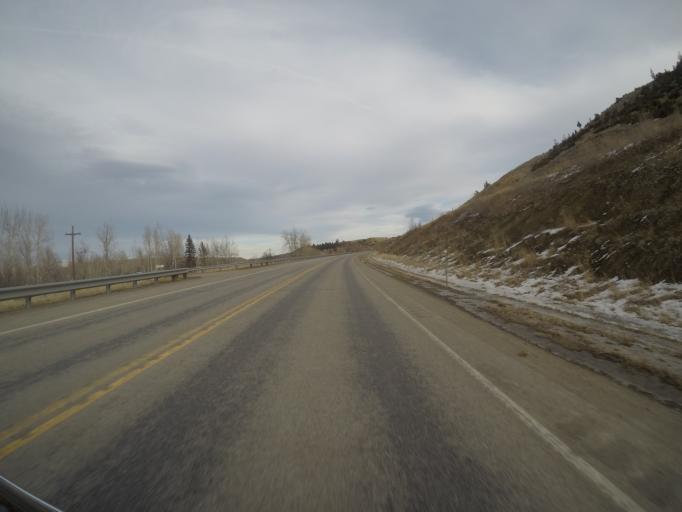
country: US
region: Montana
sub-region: Stillwater County
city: Absarokee
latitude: 45.5373
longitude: -109.4173
